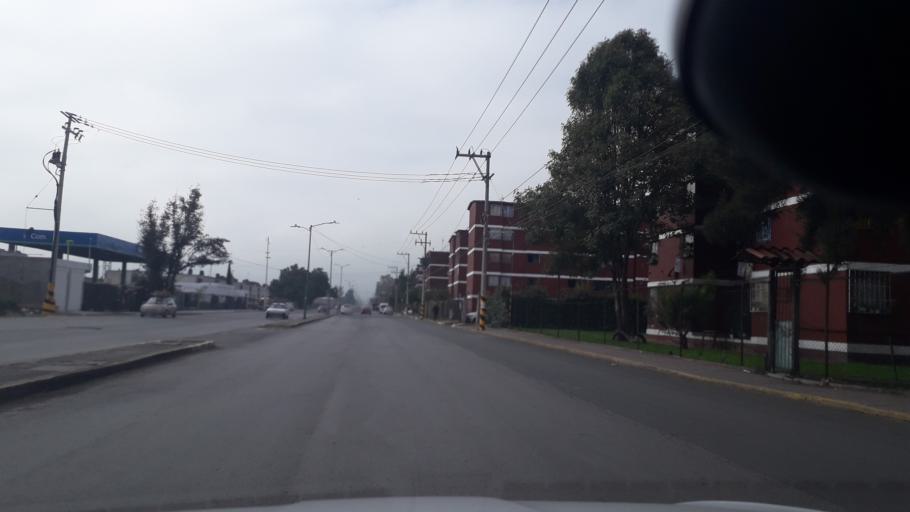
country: MX
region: Mexico
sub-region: Jaltenco
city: Alborada Jaltenco
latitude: 19.6551
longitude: -99.0764
